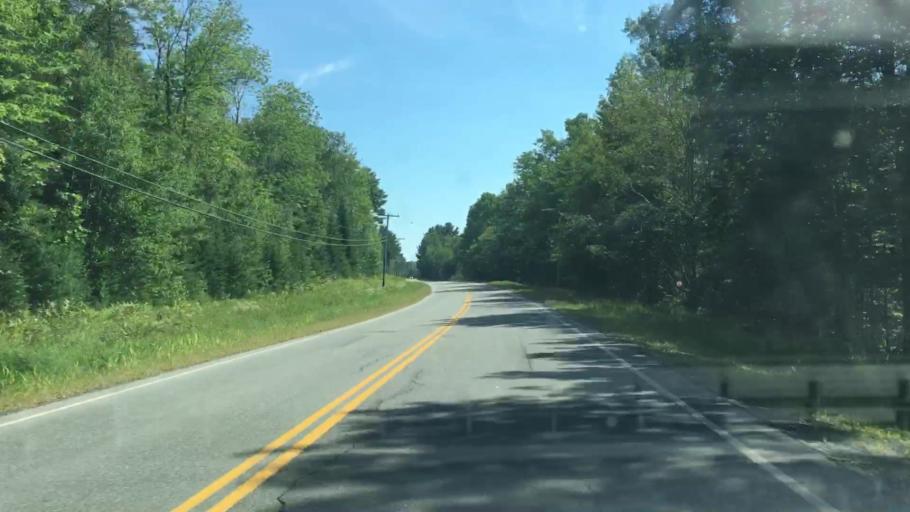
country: US
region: Maine
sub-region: Piscataquis County
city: Milo
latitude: 45.1958
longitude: -68.9029
